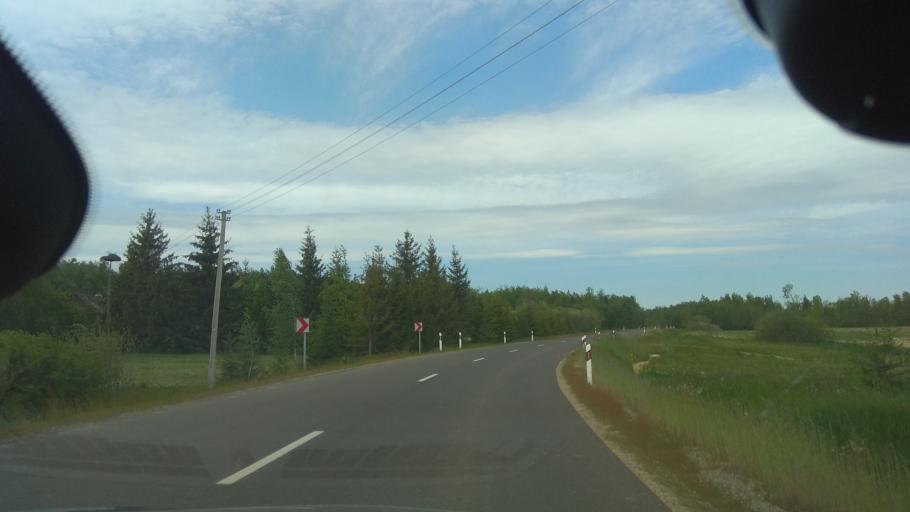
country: LT
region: Vilnius County
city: Ukmerge
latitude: 55.1084
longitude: 24.6583
